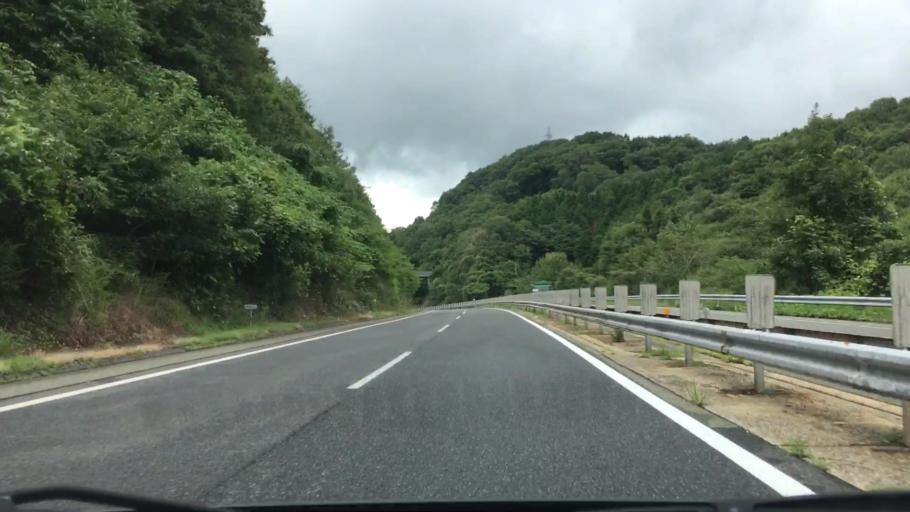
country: JP
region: Okayama
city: Niimi
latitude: 34.8884
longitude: 133.2649
